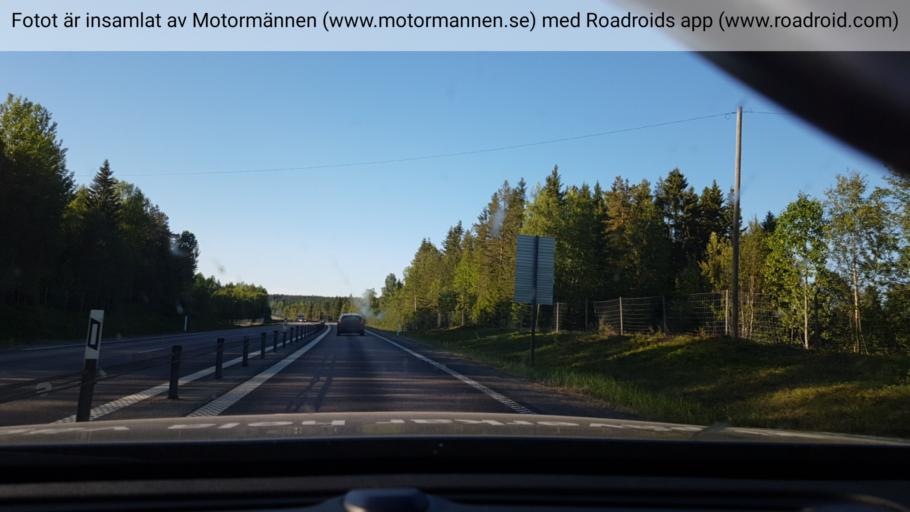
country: SE
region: Vaesternorrland
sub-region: OErnskoeldsviks Kommun
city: Husum
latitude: 63.4060
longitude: 19.2042
